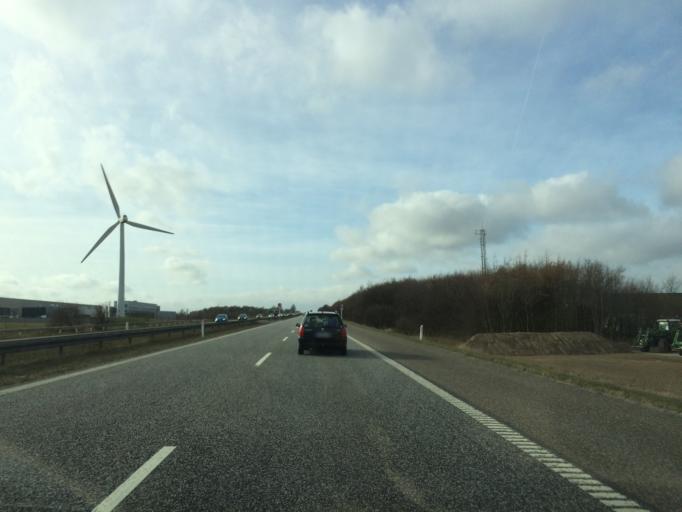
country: DK
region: Central Jutland
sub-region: Randers Kommune
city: Randers
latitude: 56.4268
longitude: 10.0475
